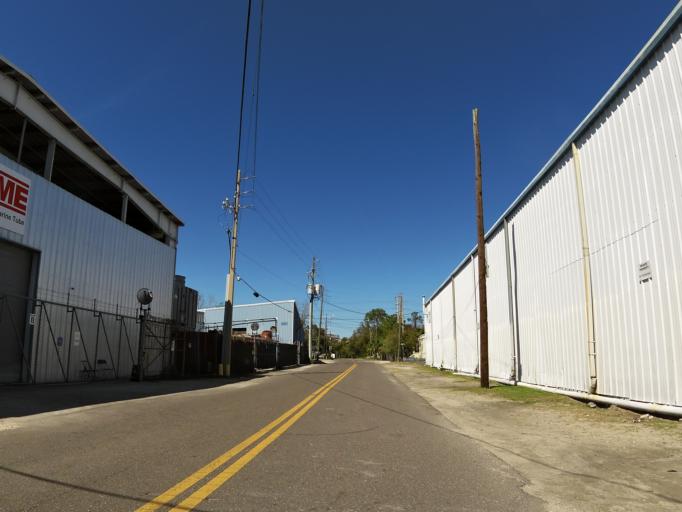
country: US
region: Florida
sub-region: Duval County
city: Jacksonville
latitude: 30.3596
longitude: -81.6431
